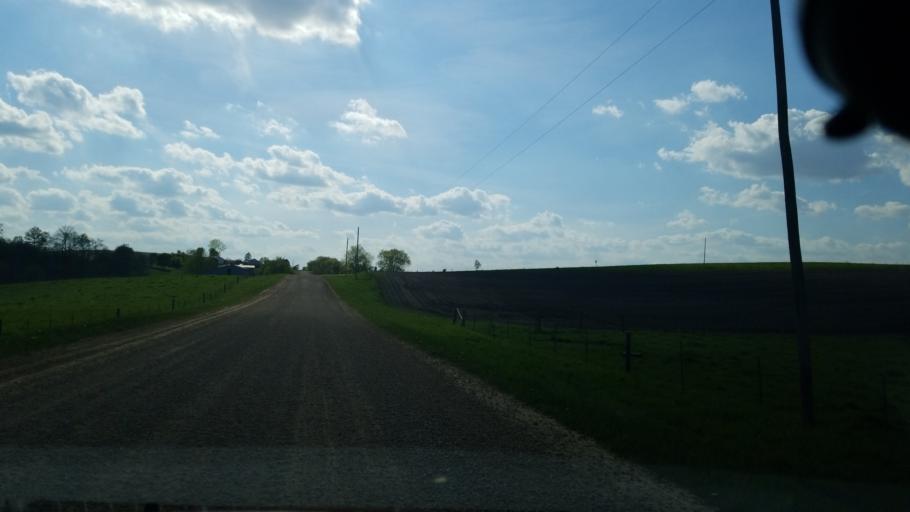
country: US
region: Iowa
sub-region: Jackson County
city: Maquoketa
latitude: 42.2149
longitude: -90.6923
